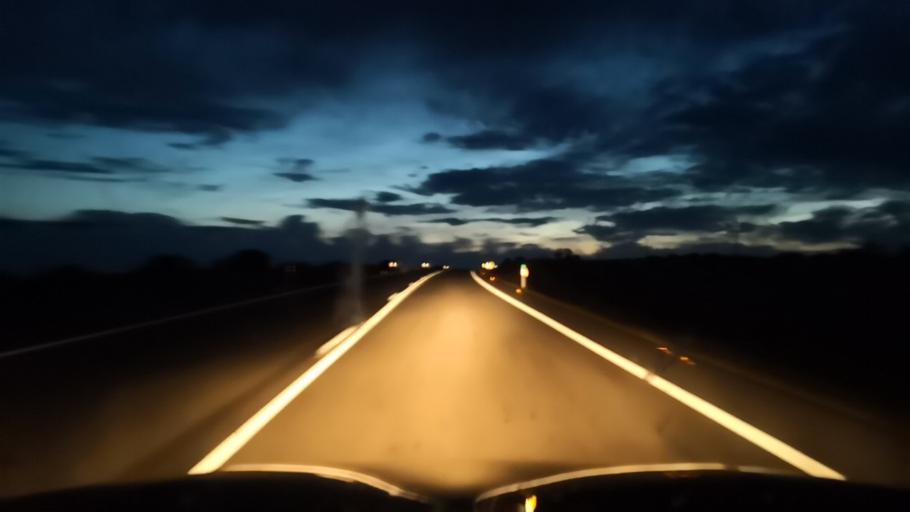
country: ES
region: Extremadura
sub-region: Provincia de Caceres
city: Carcaboso
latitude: 39.9832
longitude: -6.1732
